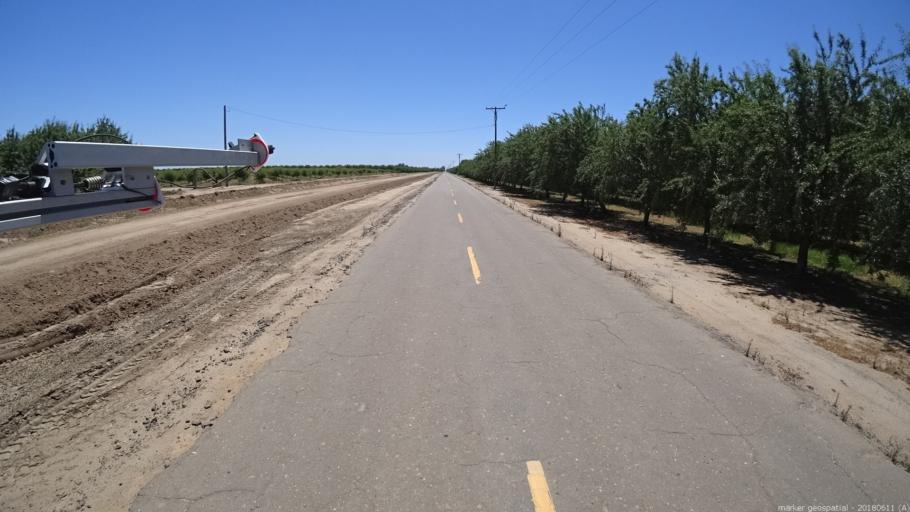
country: US
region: California
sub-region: Madera County
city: Fairmead
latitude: 37.0385
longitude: -120.1932
